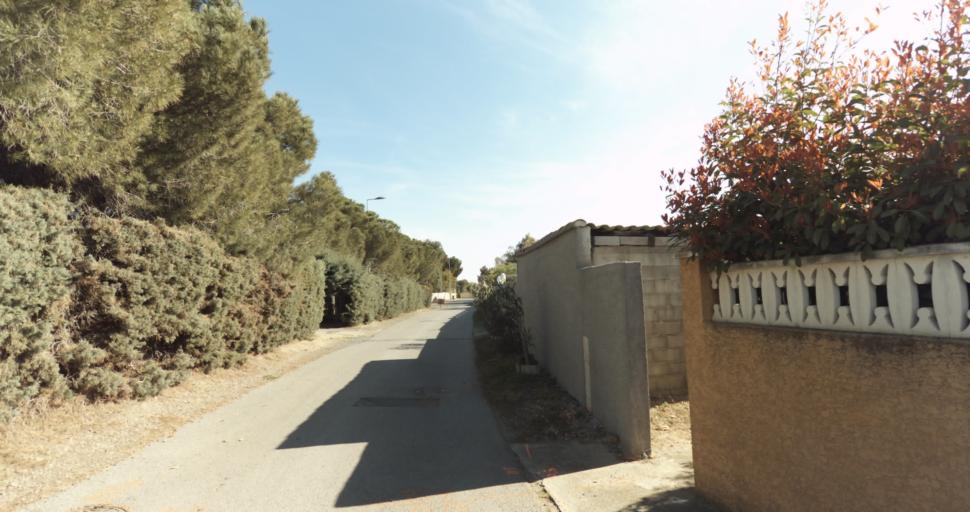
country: FR
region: Languedoc-Roussillon
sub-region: Departement de l'Herault
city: Marseillan
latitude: 43.3352
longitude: 3.5201
